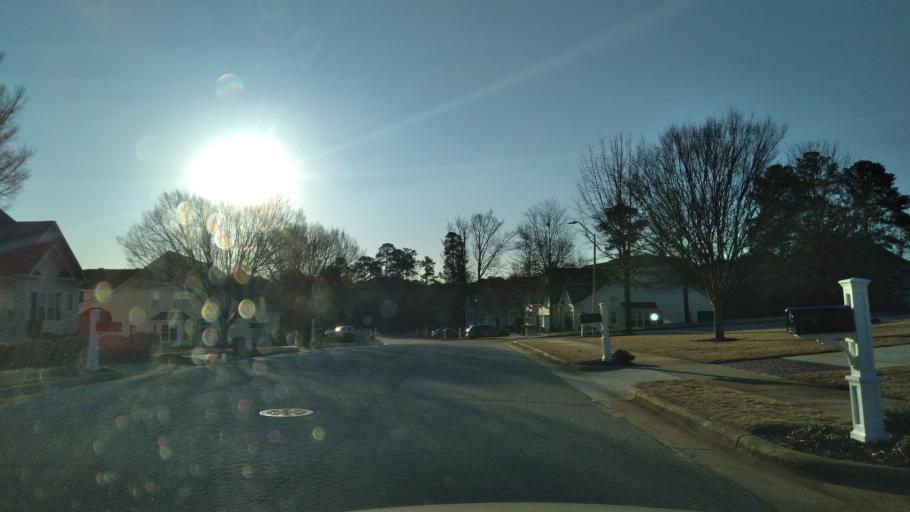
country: US
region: North Carolina
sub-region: Wake County
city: Garner
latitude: 35.6948
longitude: -78.6130
